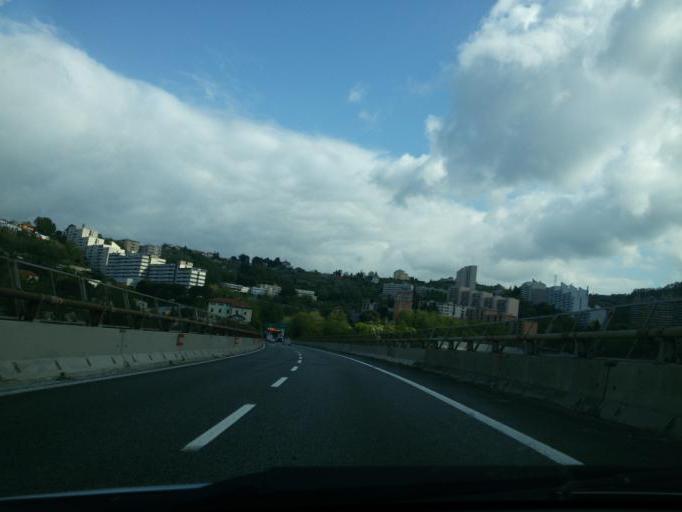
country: IT
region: Liguria
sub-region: Provincia di Genova
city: Genoa
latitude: 44.4416
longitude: 8.9039
